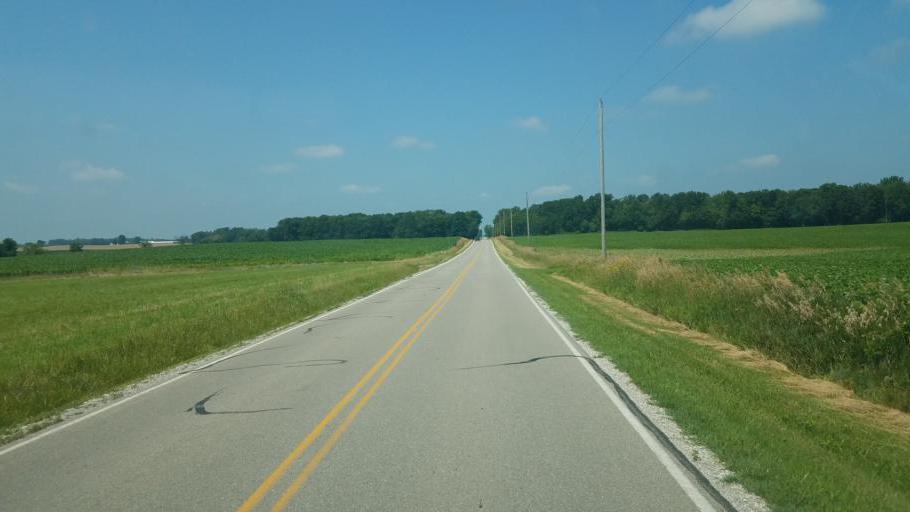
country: US
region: Ohio
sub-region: Crawford County
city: Bucyrus
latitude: 40.9937
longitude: -82.9262
